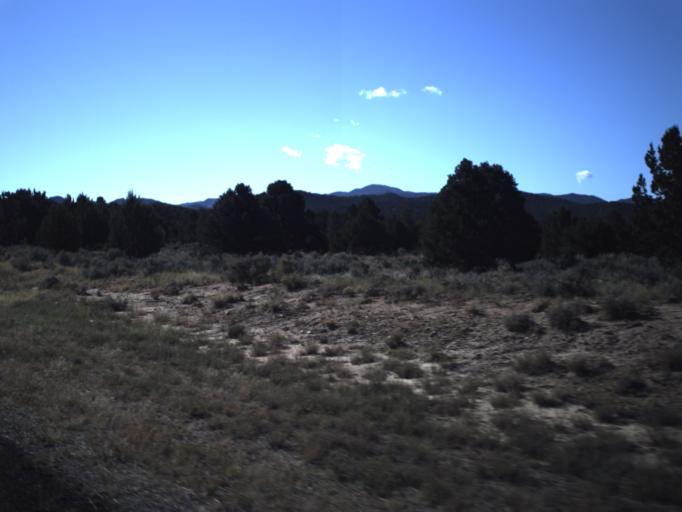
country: US
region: Utah
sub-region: Washington County
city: Enterprise
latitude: 37.6247
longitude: -113.4195
